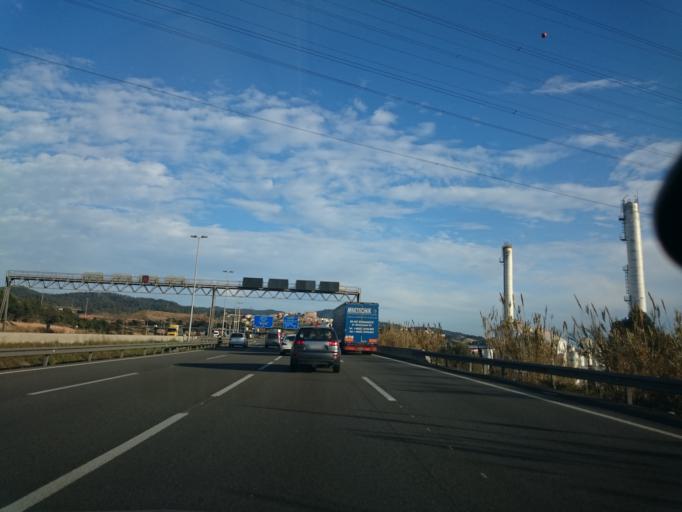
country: ES
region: Catalonia
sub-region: Provincia de Barcelona
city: Sant Andreu de la Barca
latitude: 41.4486
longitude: 1.9890
